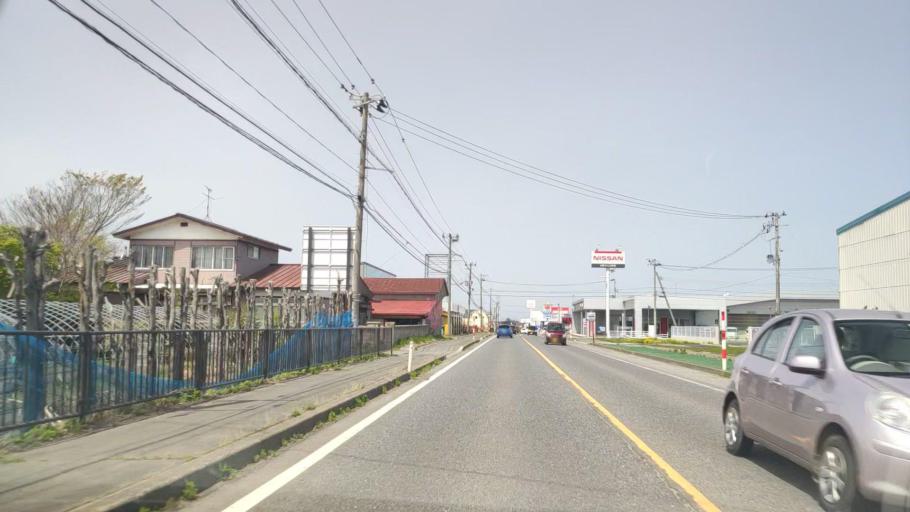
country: JP
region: Aomori
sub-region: Misawa Shi
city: Inuotose
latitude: 40.6487
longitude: 141.1968
